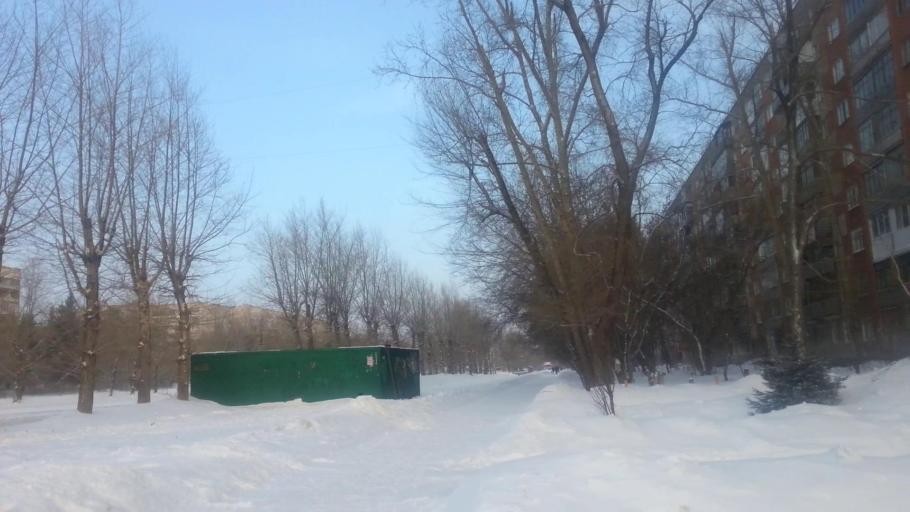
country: RU
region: Altai Krai
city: Novosilikatnyy
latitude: 53.3624
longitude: 83.6761
